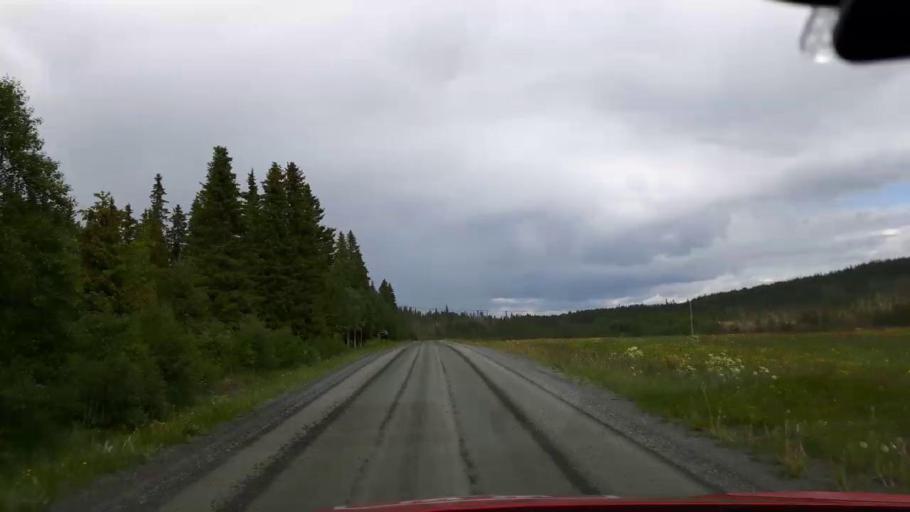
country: NO
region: Nord-Trondelag
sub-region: Lierne
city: Sandvika
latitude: 64.1473
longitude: 13.9521
